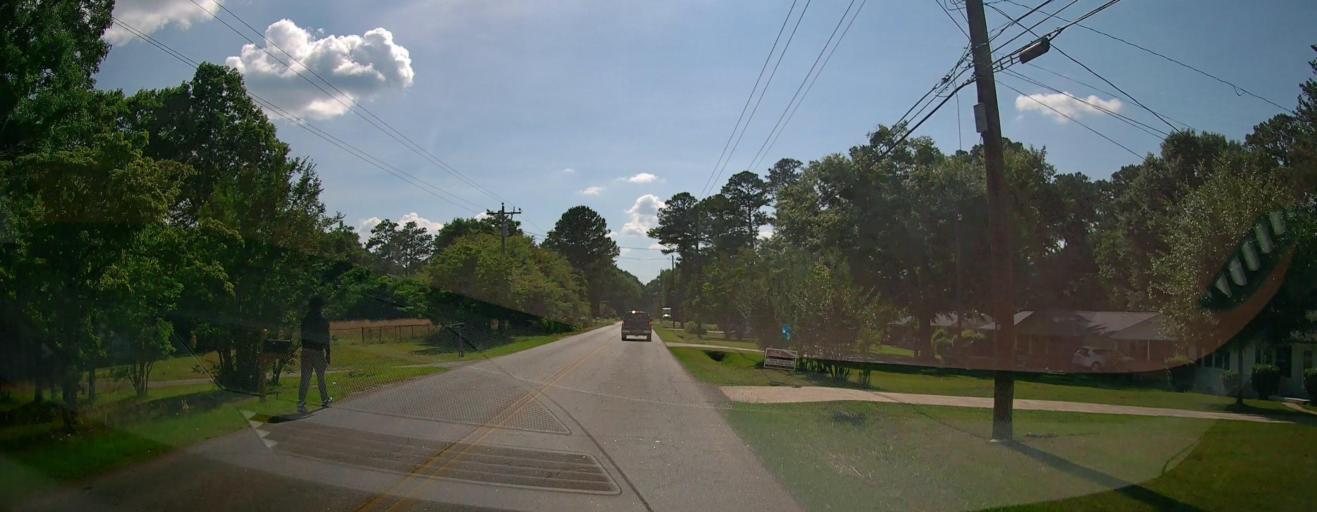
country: US
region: Georgia
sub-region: Spalding County
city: Experiment
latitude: 33.2788
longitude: -84.2704
